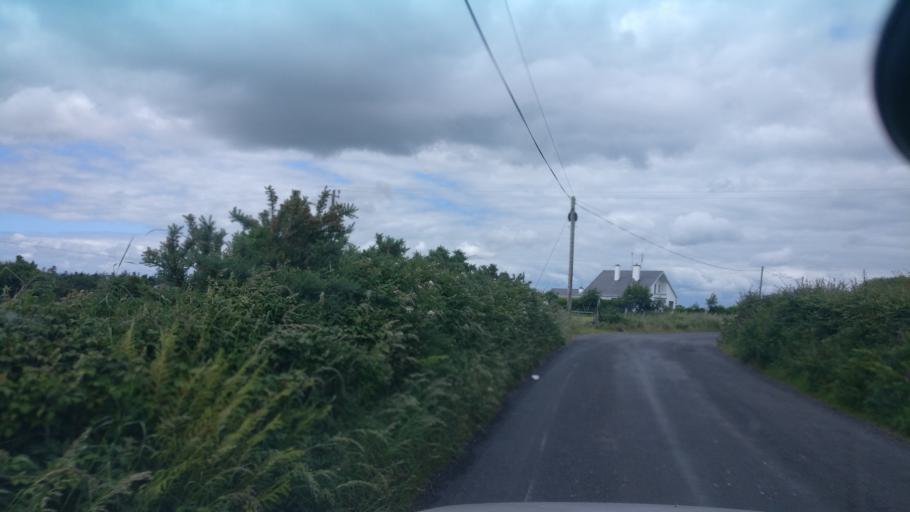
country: IE
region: Connaught
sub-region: County Galway
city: Loughrea
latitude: 53.1676
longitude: -8.5535
